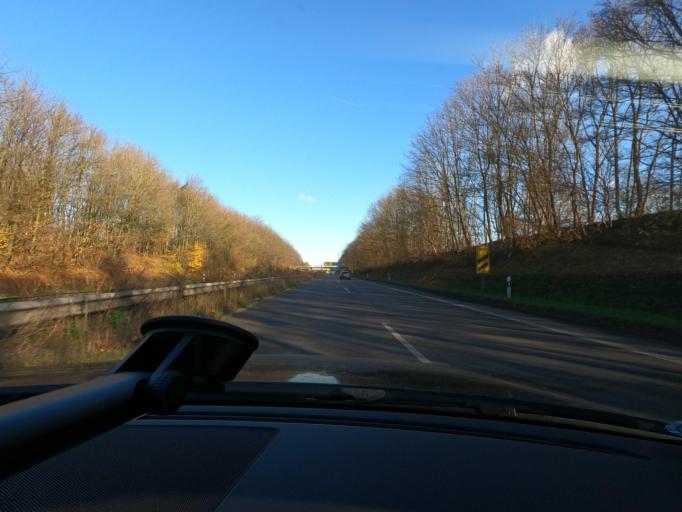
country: DE
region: North Rhine-Westphalia
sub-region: Regierungsbezirk Dusseldorf
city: Krefeld
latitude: 51.3674
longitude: 6.6180
